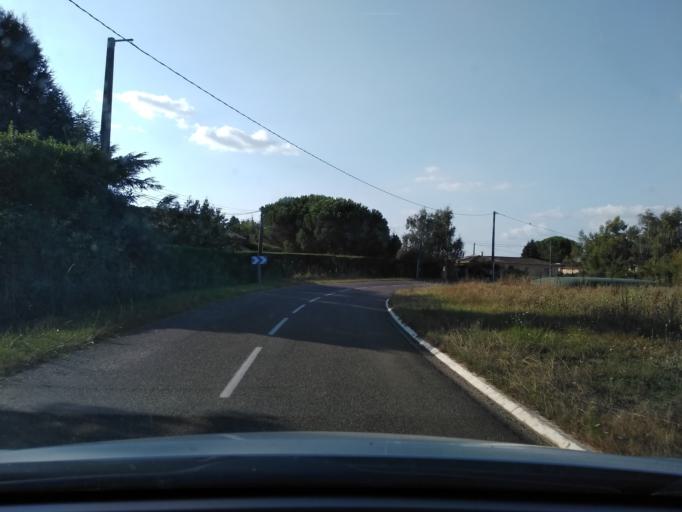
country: FR
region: Midi-Pyrenees
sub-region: Departement du Tarn-et-Garonne
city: Montech
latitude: 43.9740
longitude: 1.2441
